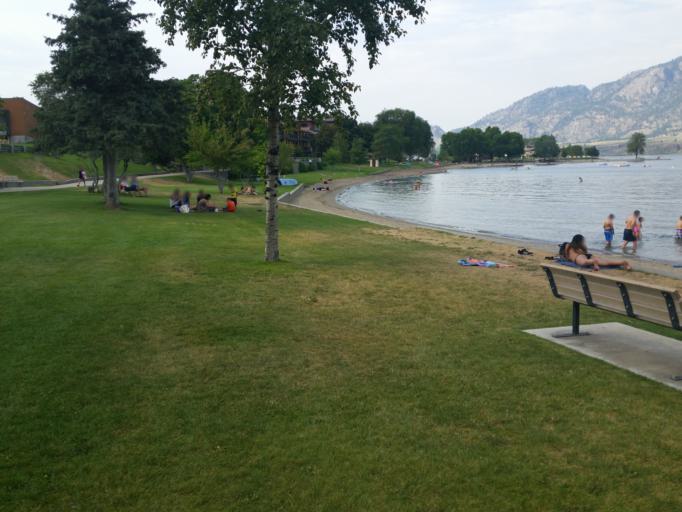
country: CA
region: British Columbia
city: Osoyoos
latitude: 49.0295
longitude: -119.4609
